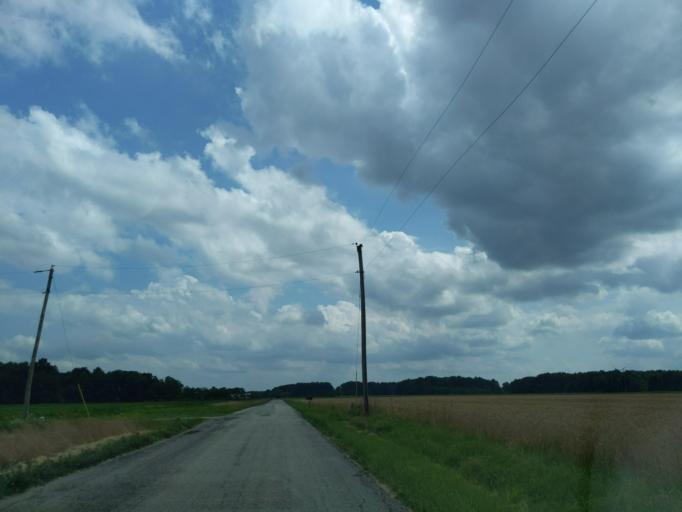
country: US
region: Indiana
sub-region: Ripley County
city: Batesville
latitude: 39.3144
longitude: -85.1896
